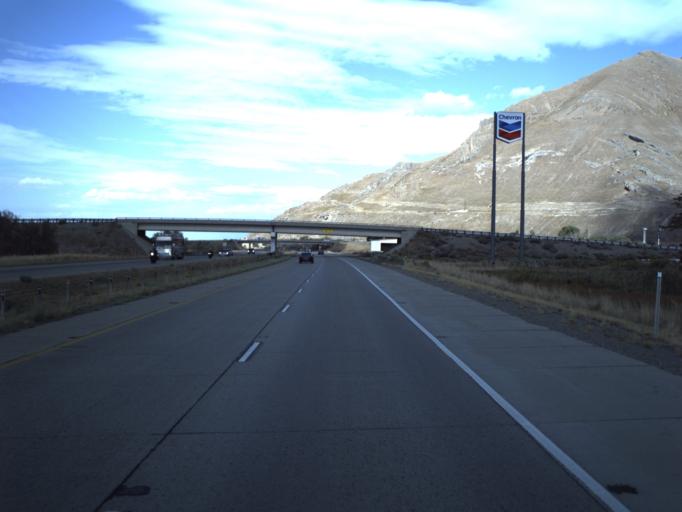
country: US
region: Utah
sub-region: Tooele County
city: Stansbury park
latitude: 40.6887
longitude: -112.2682
